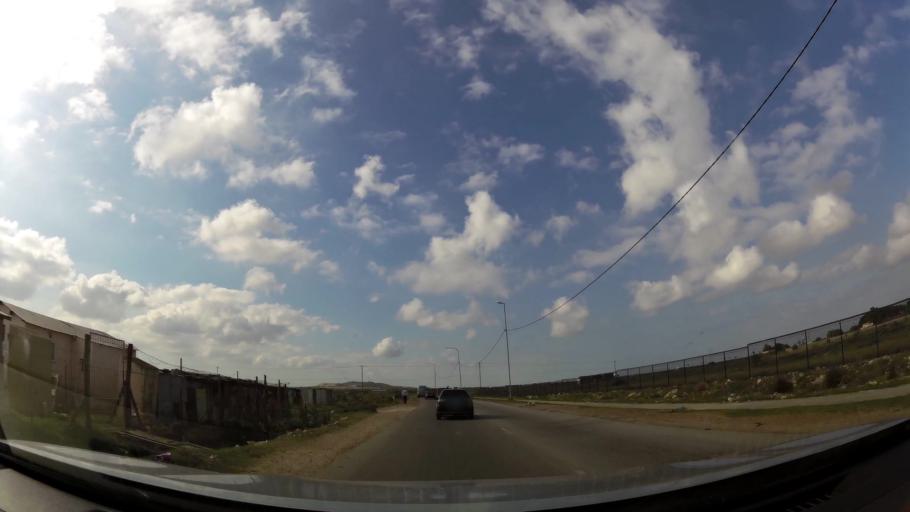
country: ZA
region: Eastern Cape
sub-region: Nelson Mandela Bay Metropolitan Municipality
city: Port Elizabeth
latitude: -33.7858
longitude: 25.5913
